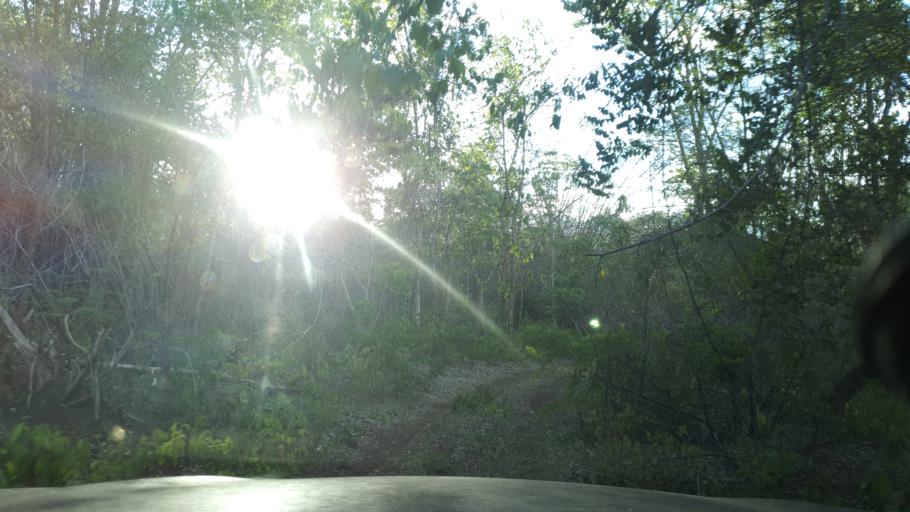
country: TH
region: Lampang
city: Sop Prap
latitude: 17.9648
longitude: 99.3516
